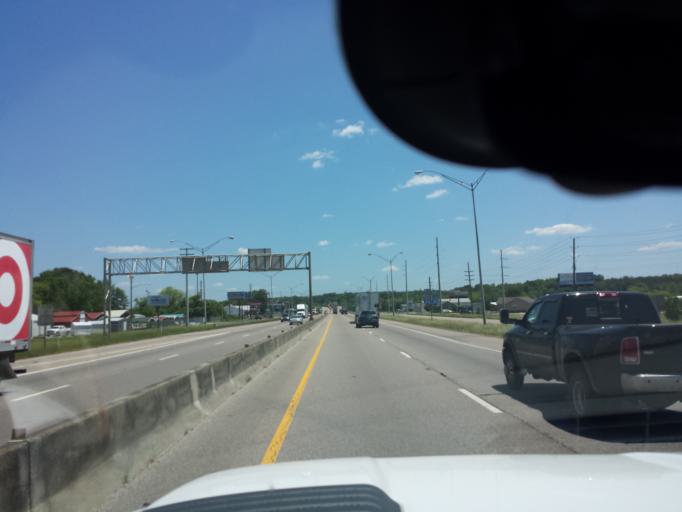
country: US
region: Mississippi
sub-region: Lauderdale County
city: Meridian
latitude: 32.3490
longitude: -88.7079
